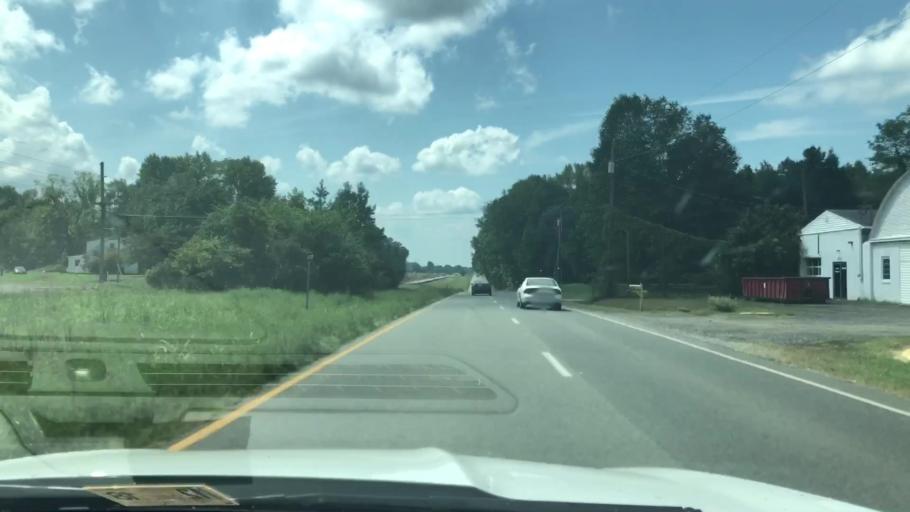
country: US
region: Virginia
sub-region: Richmond County
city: Warsaw
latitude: 37.9646
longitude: -76.8012
